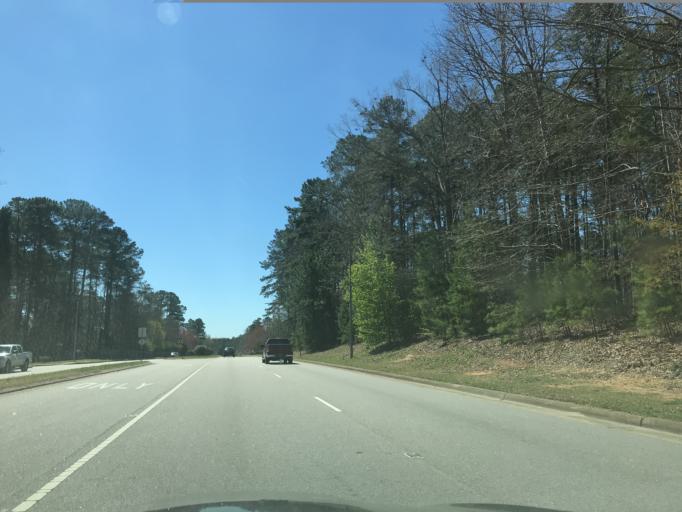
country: US
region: North Carolina
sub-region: Wake County
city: Garner
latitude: 35.7048
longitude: -78.6410
